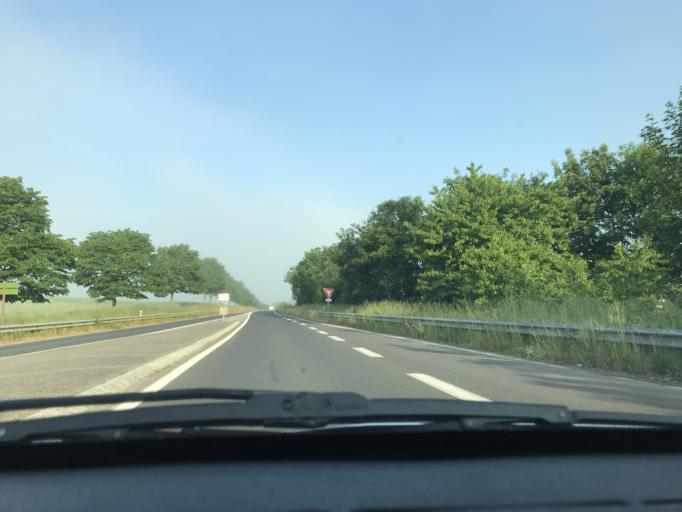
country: FR
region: Lorraine
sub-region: Departement de la Moselle
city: Vic-sur-Seille
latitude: 48.7748
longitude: 6.5276
